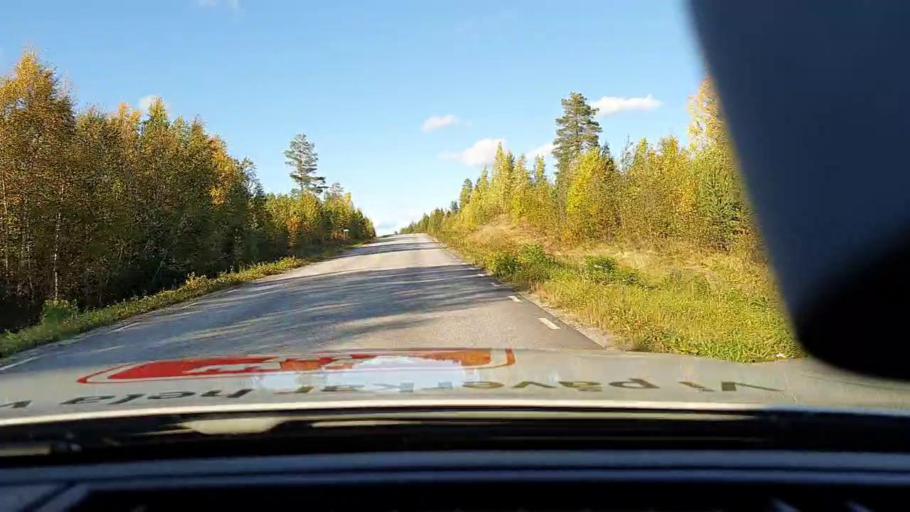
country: SE
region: Norrbotten
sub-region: Pitea Kommun
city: Norrfjarden
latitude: 65.4936
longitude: 21.4739
